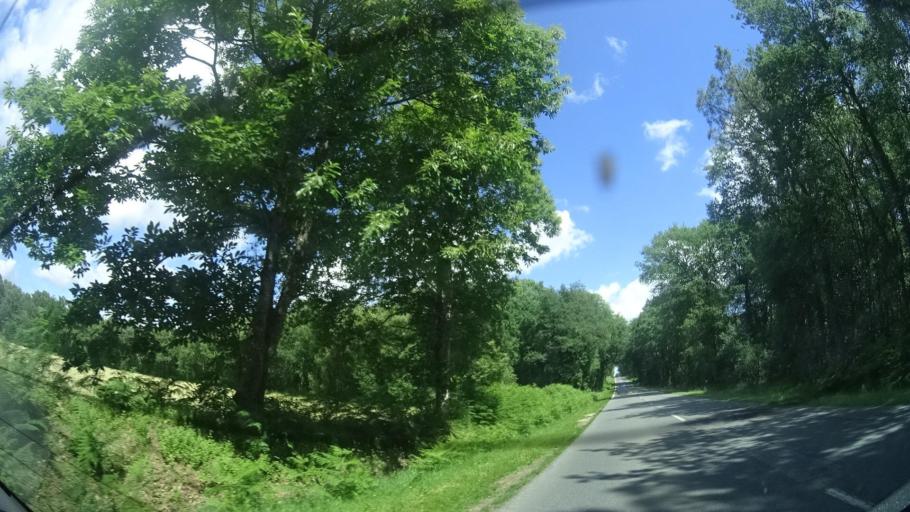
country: FR
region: Brittany
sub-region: Departement du Morbihan
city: Pluherlin
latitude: 47.6768
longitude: -2.3791
